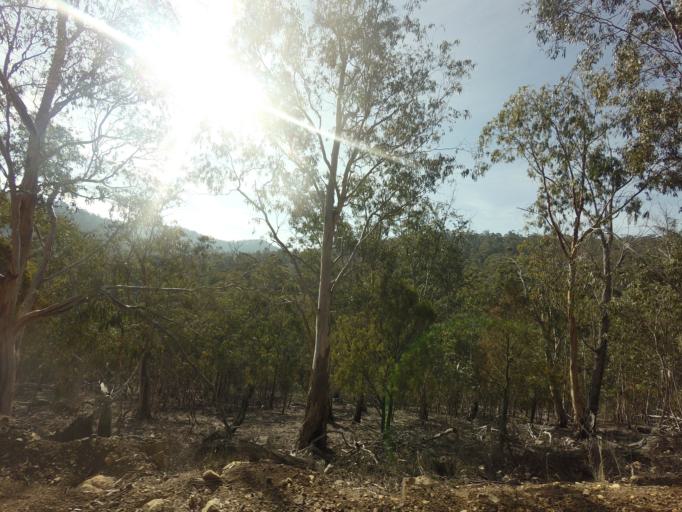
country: AU
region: Tasmania
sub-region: Sorell
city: Sorell
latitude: -42.5270
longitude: 147.4575
